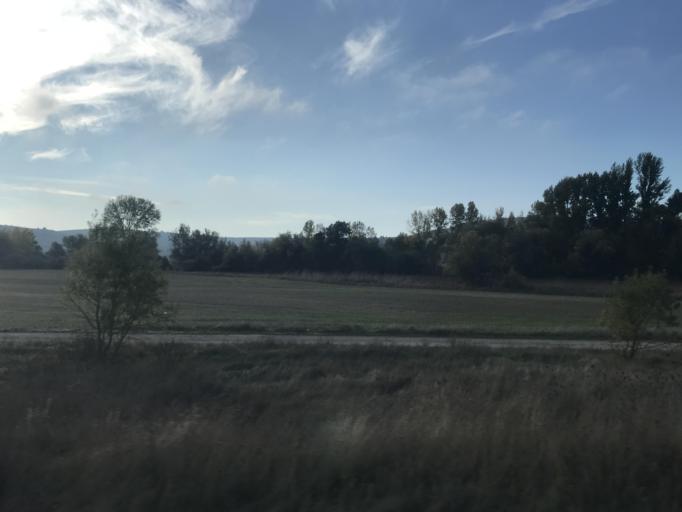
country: ES
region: Castille and Leon
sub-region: Provincia de Burgos
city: Celada del Camino
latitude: 42.2563
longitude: -3.9361
